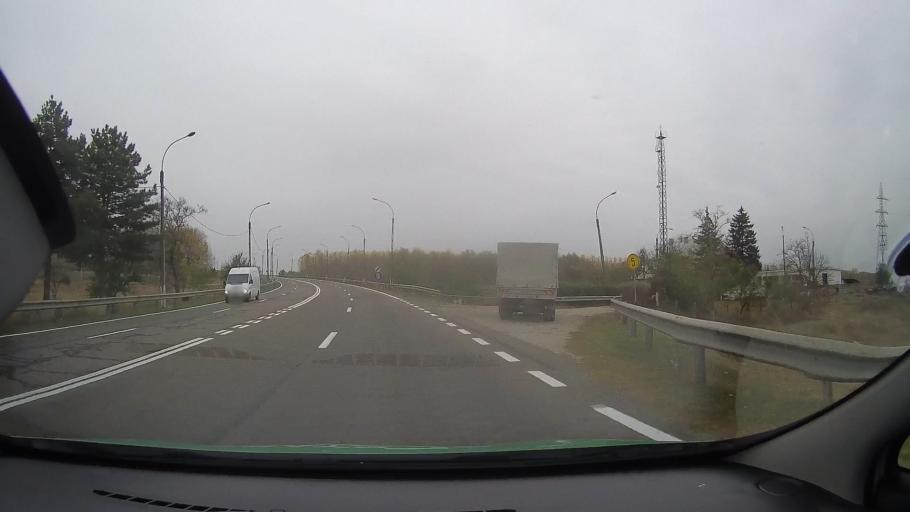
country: RO
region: Ialomita
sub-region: Comuna Giurgeni
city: Giurgeni
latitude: 44.7515
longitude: 27.8909
